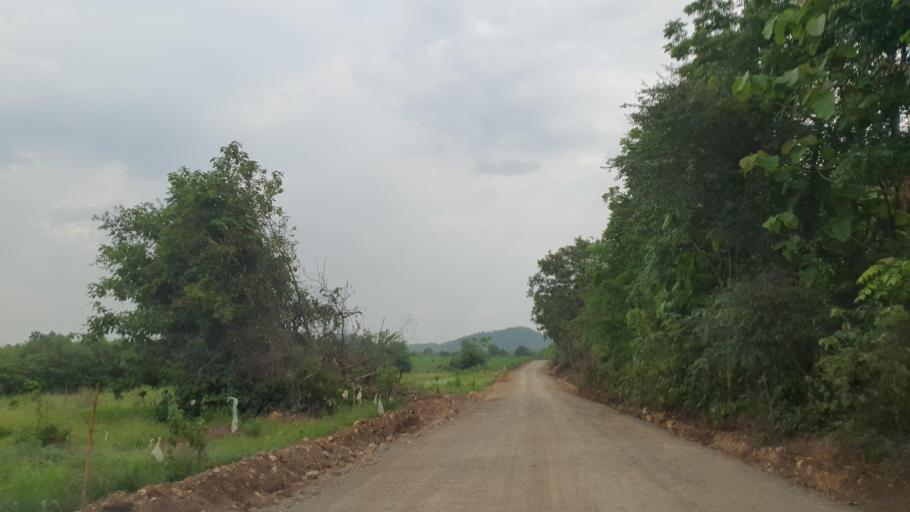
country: TH
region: Sukhothai
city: Thung Saliam
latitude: 17.2580
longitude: 99.5400
